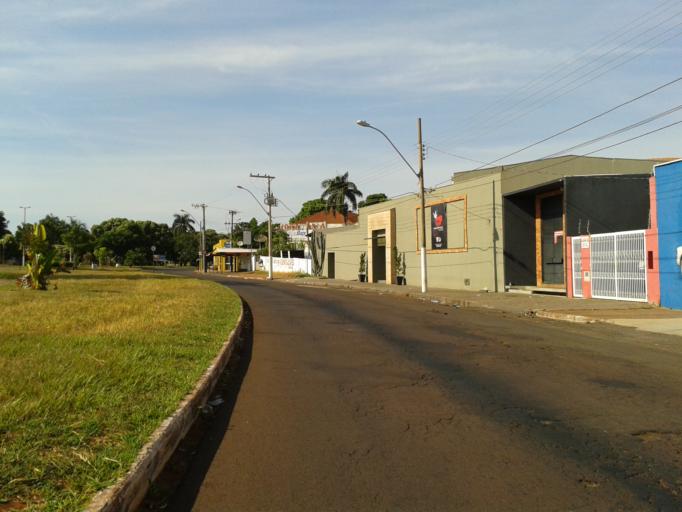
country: BR
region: Minas Gerais
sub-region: Ituiutaba
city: Ituiutaba
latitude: -18.9678
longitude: -49.4605
